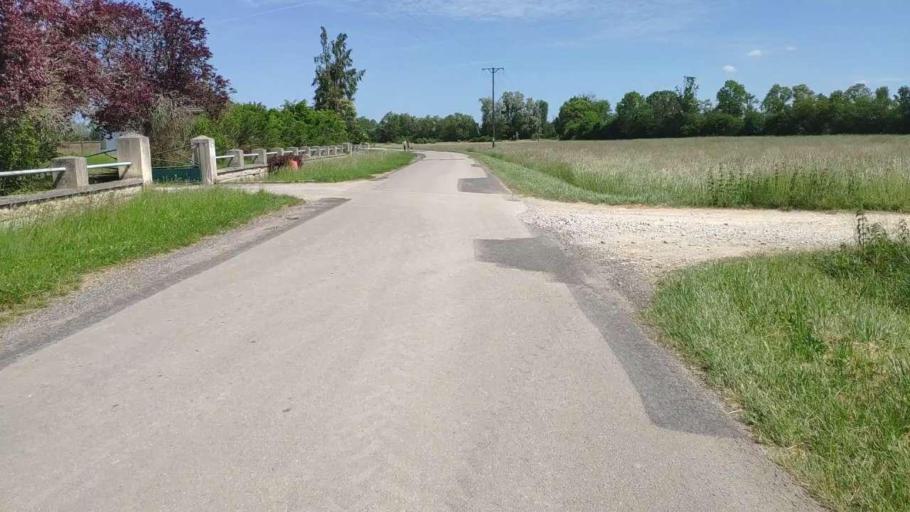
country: FR
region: Franche-Comte
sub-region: Departement du Jura
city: Bletterans
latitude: 46.7217
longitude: 5.4446
